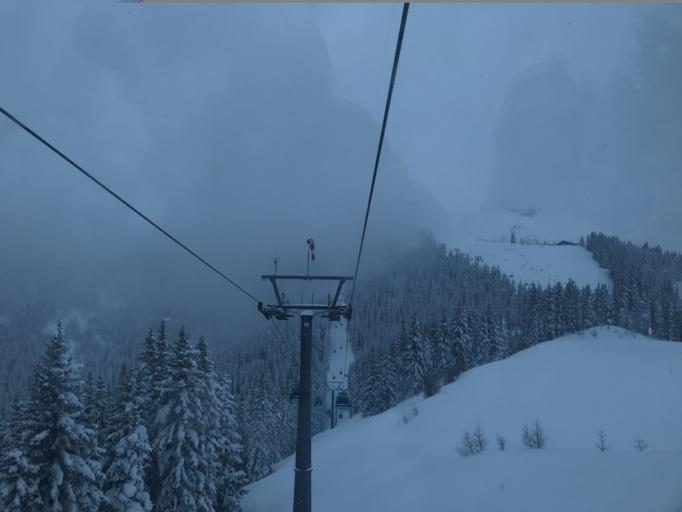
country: AT
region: Salzburg
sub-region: Politischer Bezirk Zell am See
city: Kaprun
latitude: 47.3163
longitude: 12.7490
